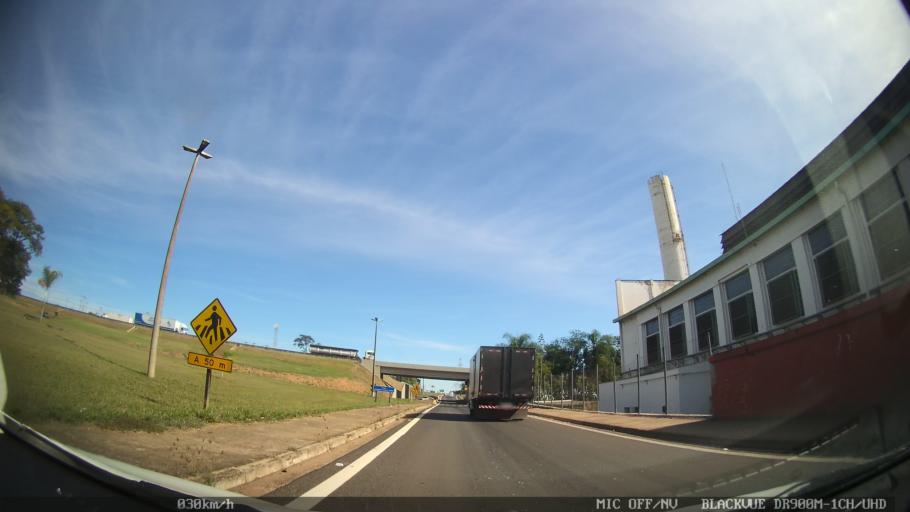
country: BR
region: Sao Paulo
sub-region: Porto Ferreira
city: Porto Ferreira
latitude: -21.8507
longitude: -47.4940
